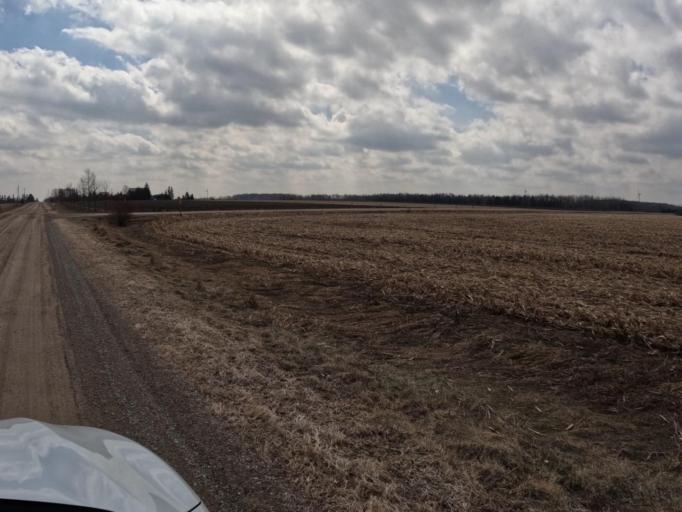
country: CA
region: Ontario
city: Shelburne
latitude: 44.0241
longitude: -80.3305
